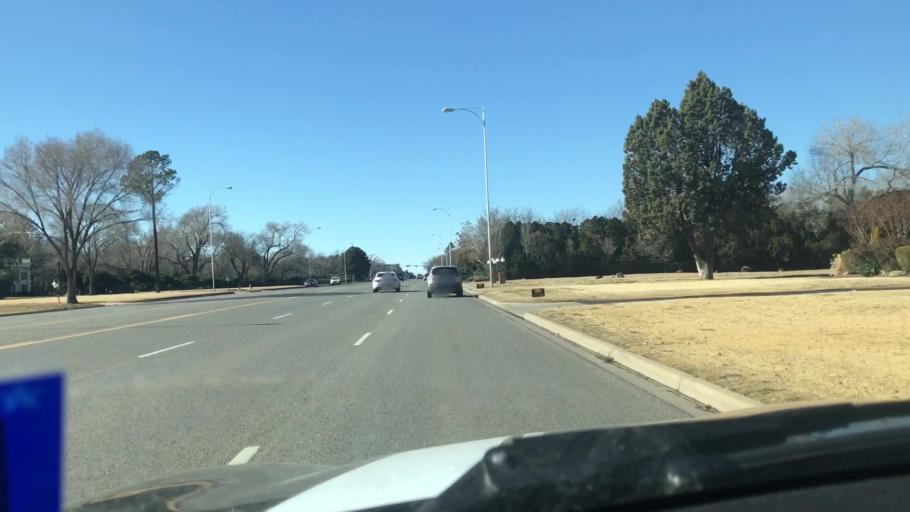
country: US
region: Texas
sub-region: Lubbock County
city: Lubbock
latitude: 33.5779
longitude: -101.9185
